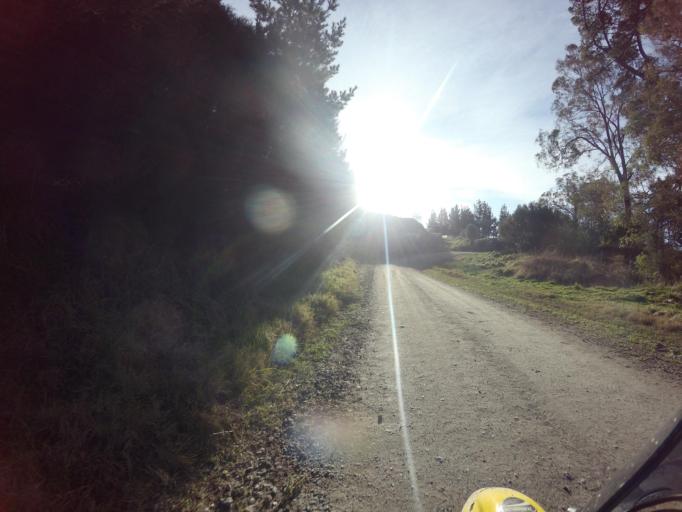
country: NZ
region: Hawke's Bay
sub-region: Wairoa District
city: Wairoa
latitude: -38.7435
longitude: 177.5206
